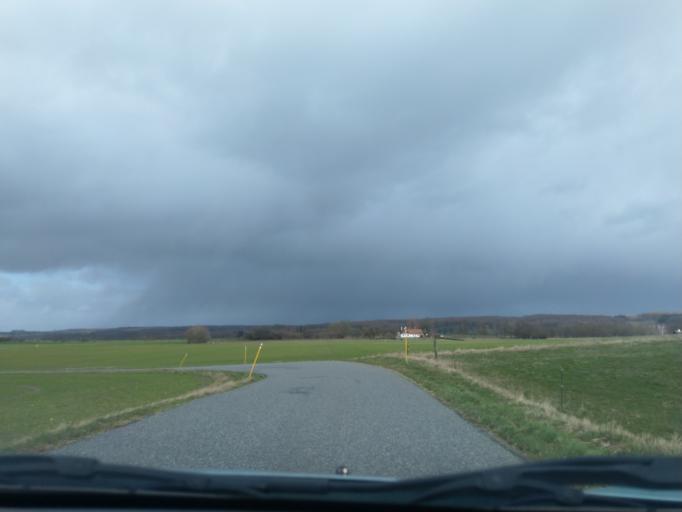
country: DK
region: Zealand
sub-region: Naestved Kommune
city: Fuglebjerg
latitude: 55.3475
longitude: 11.5839
